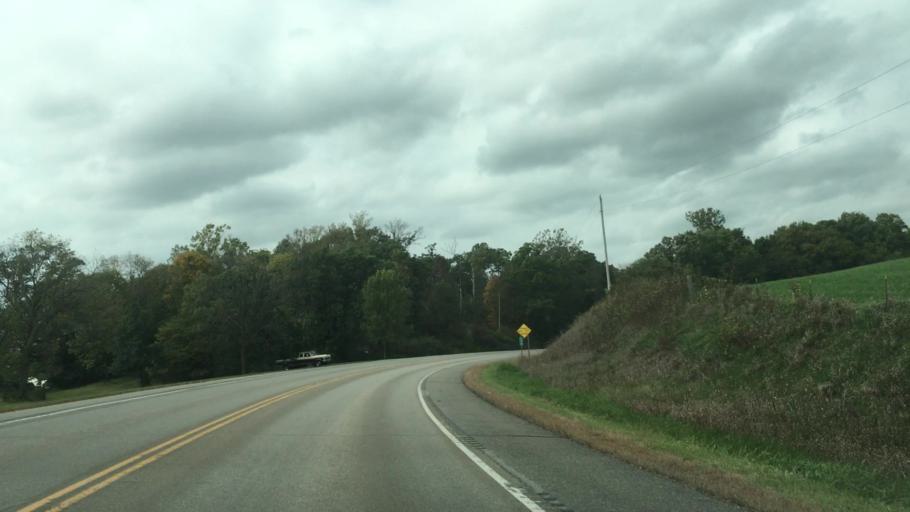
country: US
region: Minnesota
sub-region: Fillmore County
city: Chatfield
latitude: 43.8048
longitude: -92.1329
